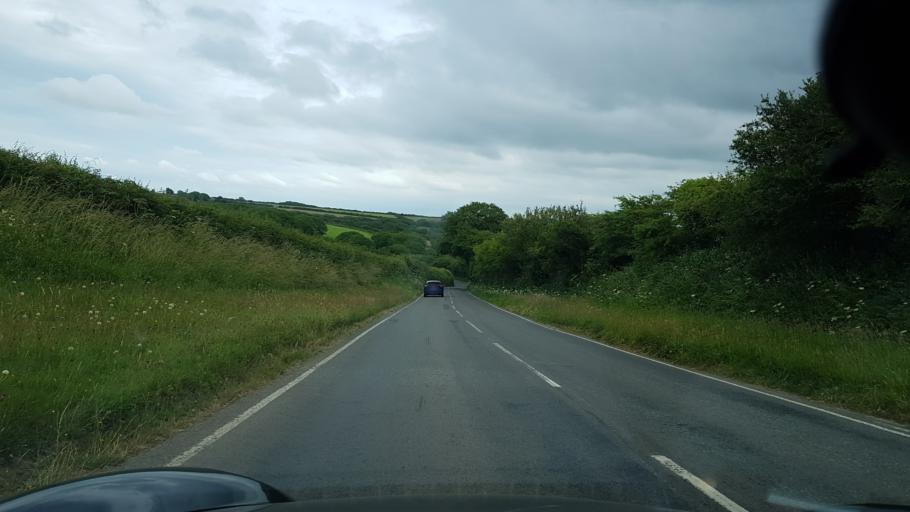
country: GB
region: Wales
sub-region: Pembrokeshire
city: Herbrandston
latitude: 51.7651
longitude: -5.0808
